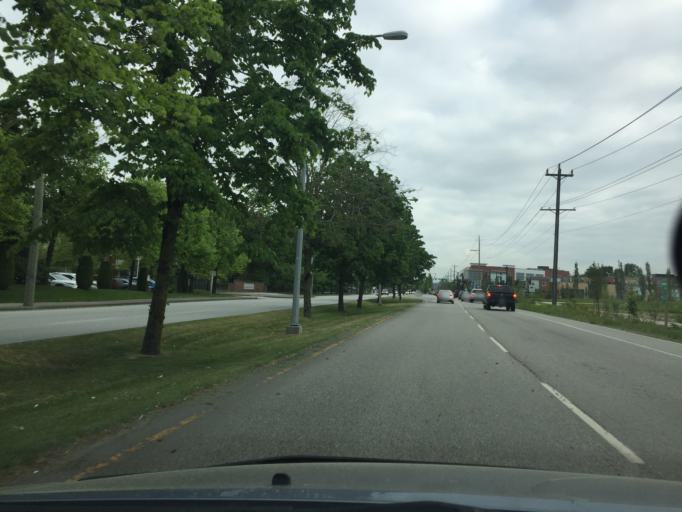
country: CA
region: British Columbia
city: Richmond
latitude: 49.1751
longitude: -123.1246
